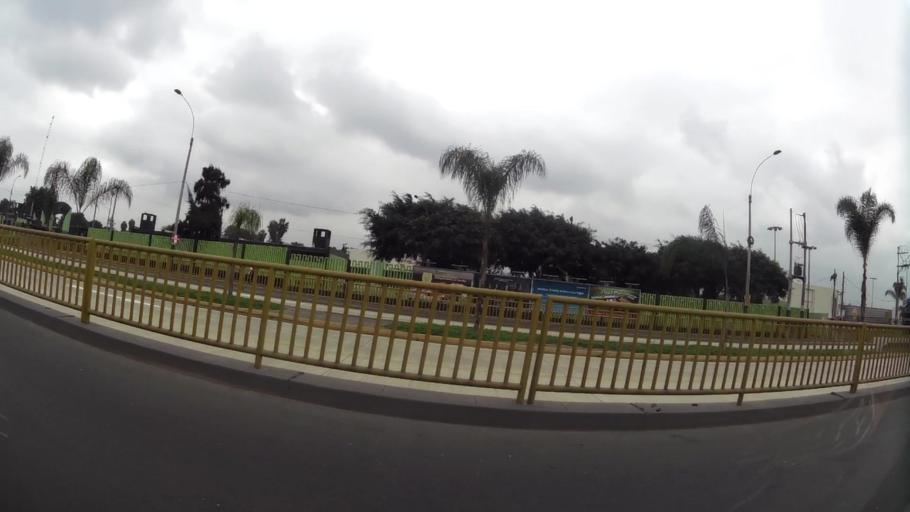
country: PE
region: Lima
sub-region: Lima
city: Surco
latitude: -12.1724
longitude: -77.0159
